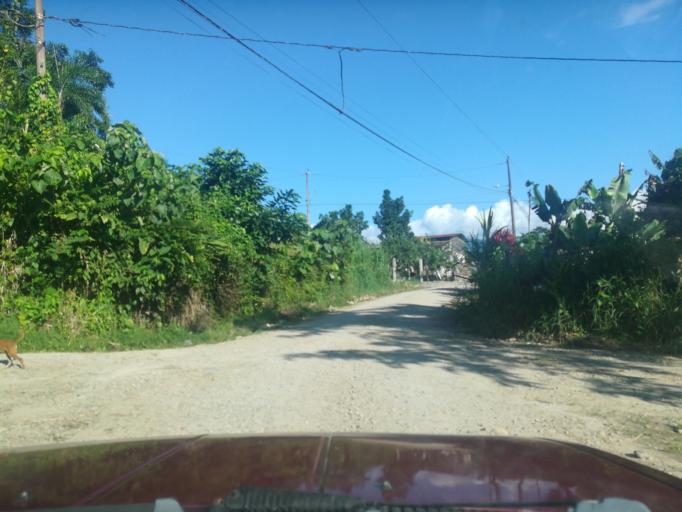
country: EC
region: Napo
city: Tena
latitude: -0.9922
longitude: -77.8323
